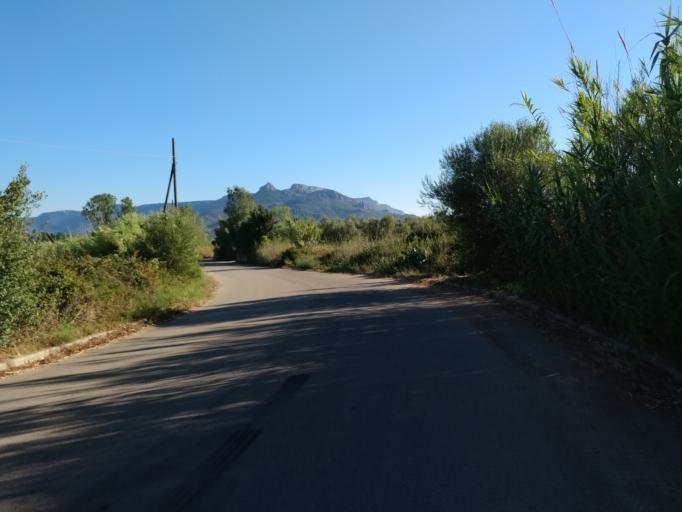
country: IT
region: Sardinia
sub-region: Provincia di Ogliastra
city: Girasole
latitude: 39.9530
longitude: 9.6715
